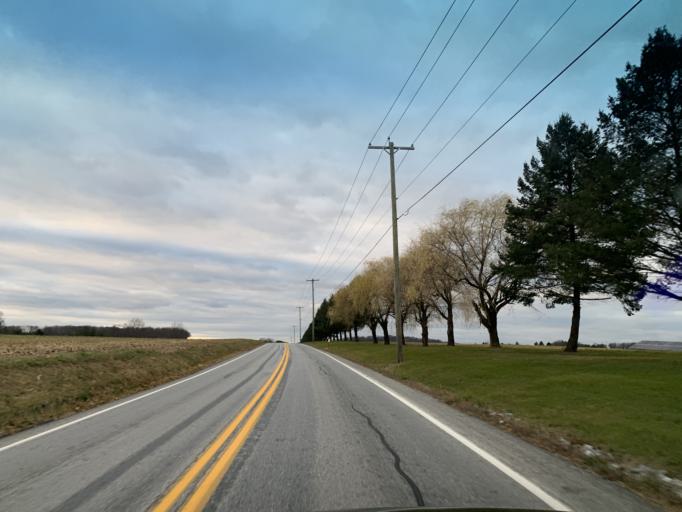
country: US
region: Pennsylvania
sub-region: York County
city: Stewartstown
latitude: 39.7793
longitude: -76.6109
